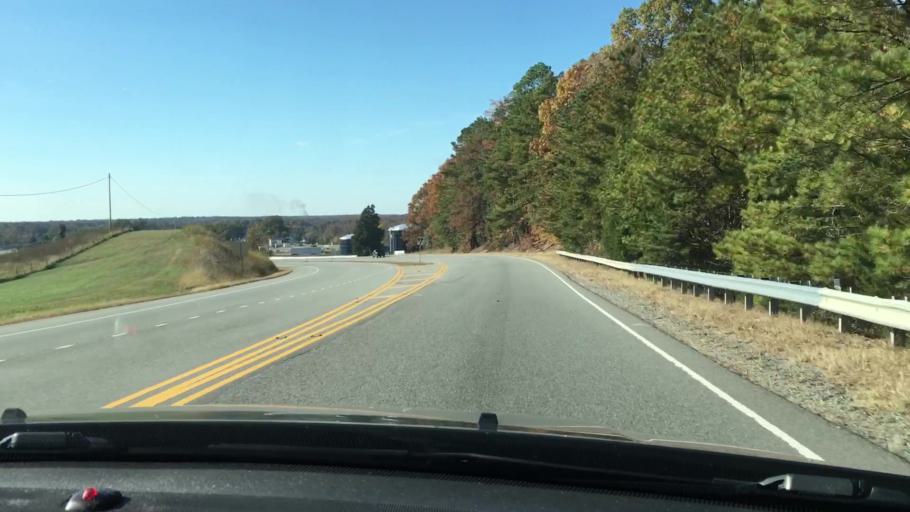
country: US
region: Virginia
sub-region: Hanover County
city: Hanover
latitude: 37.8510
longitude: -77.4096
